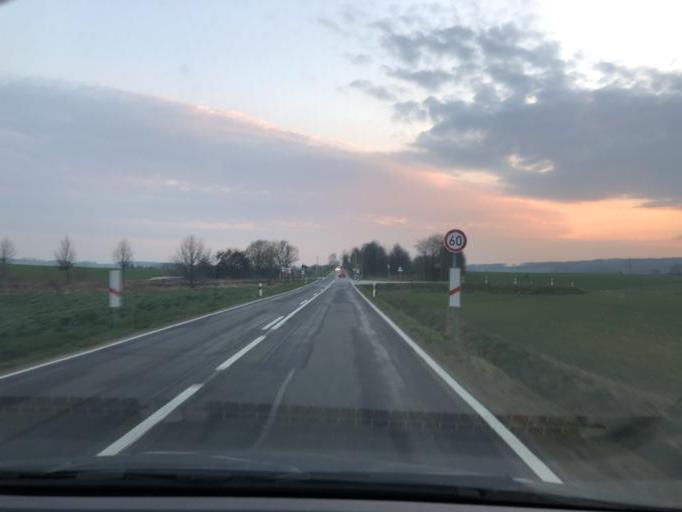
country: DE
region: Saxony
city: Haselbachtal
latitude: 51.2380
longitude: 14.0563
